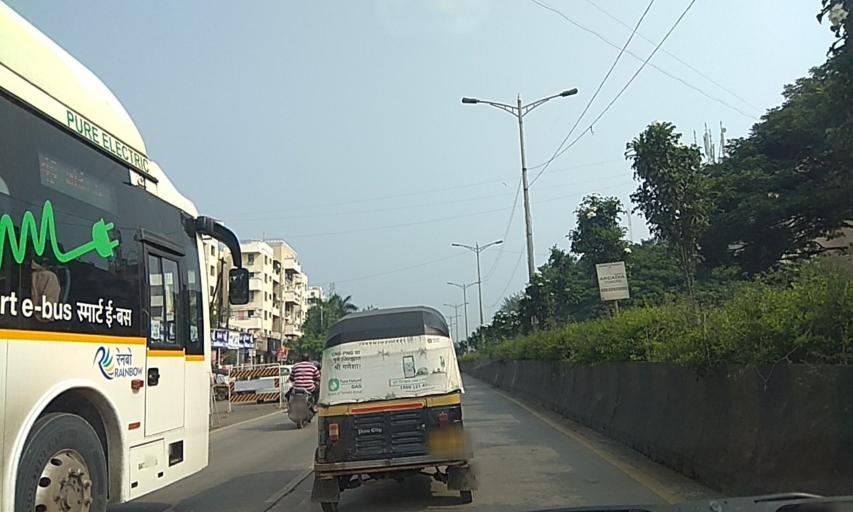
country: IN
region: Maharashtra
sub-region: Pune Division
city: Lohogaon
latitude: 18.5588
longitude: 73.9382
